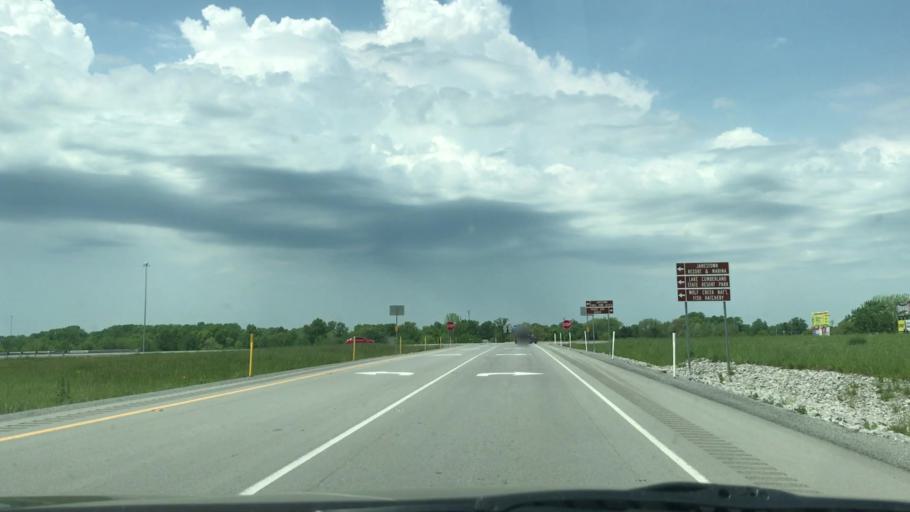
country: US
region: Kentucky
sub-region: Russell County
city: Russell Springs
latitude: 37.0530
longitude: -85.0687
